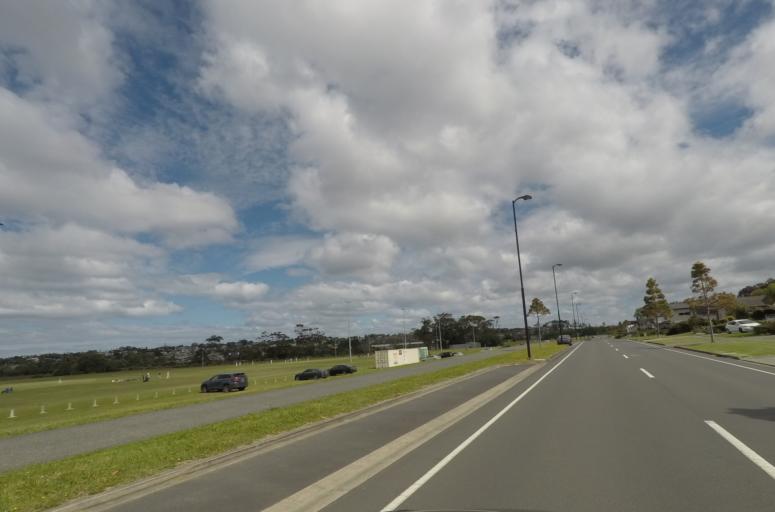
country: NZ
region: Auckland
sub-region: Auckland
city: Rothesay Bay
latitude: -36.5998
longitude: 174.6788
